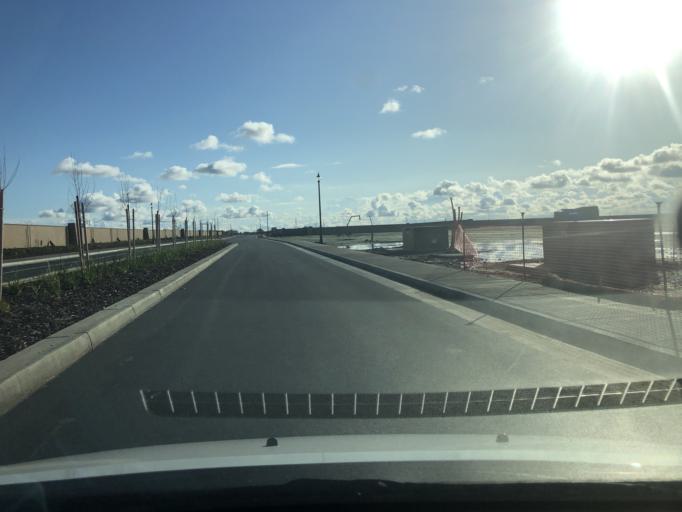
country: US
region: California
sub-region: Sacramento County
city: Elverta
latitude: 38.7752
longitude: -121.3972
